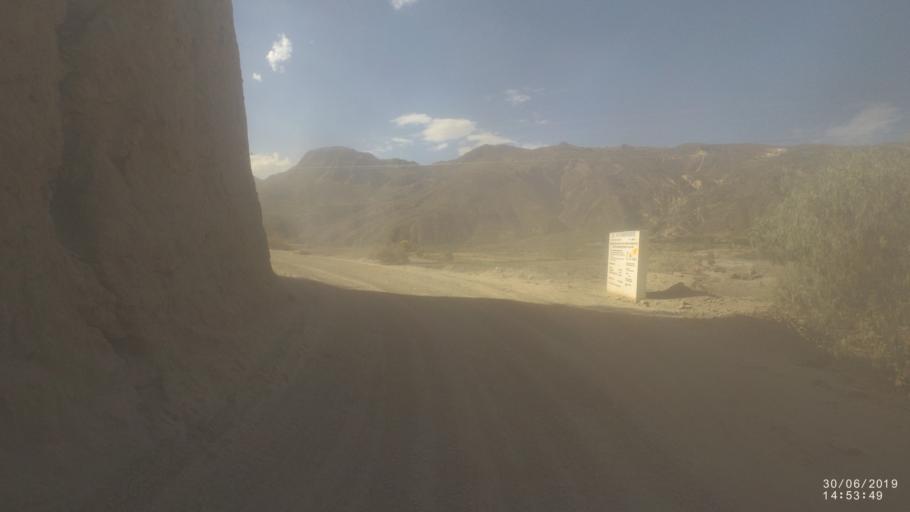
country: BO
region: Cochabamba
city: Irpa Irpa
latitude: -17.7616
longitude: -66.3495
